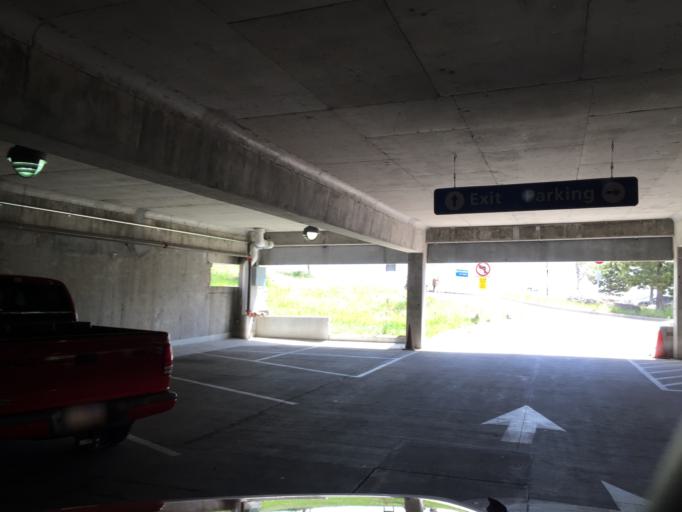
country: US
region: South Dakota
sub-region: Custer County
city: Custer
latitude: 43.8759
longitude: -103.4526
